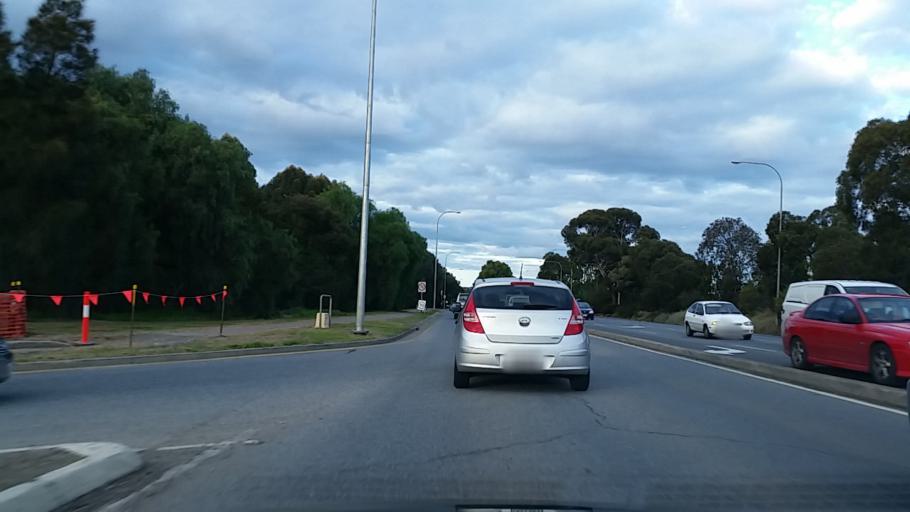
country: AU
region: South Australia
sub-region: Salisbury
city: Ingle Farm
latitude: -34.8245
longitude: 138.6181
